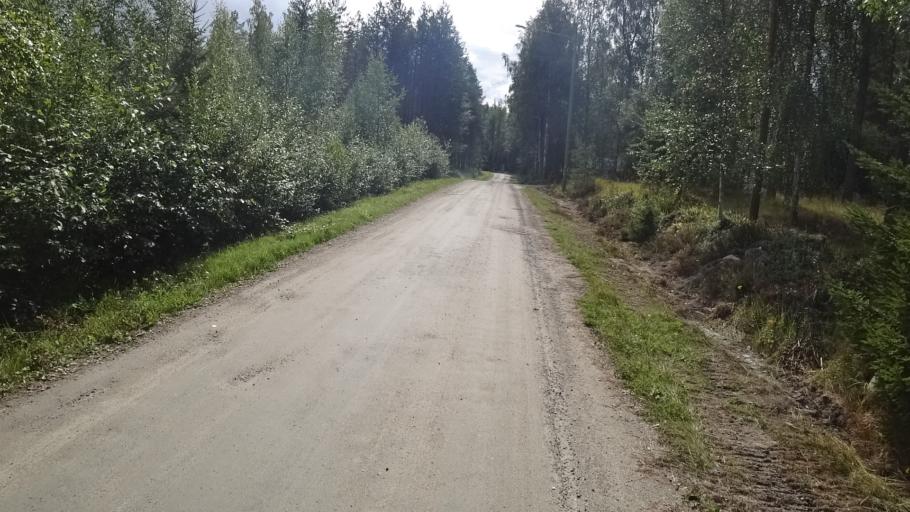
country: FI
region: North Karelia
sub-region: Joensuu
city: Ilomantsi
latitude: 62.6334
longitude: 31.2769
